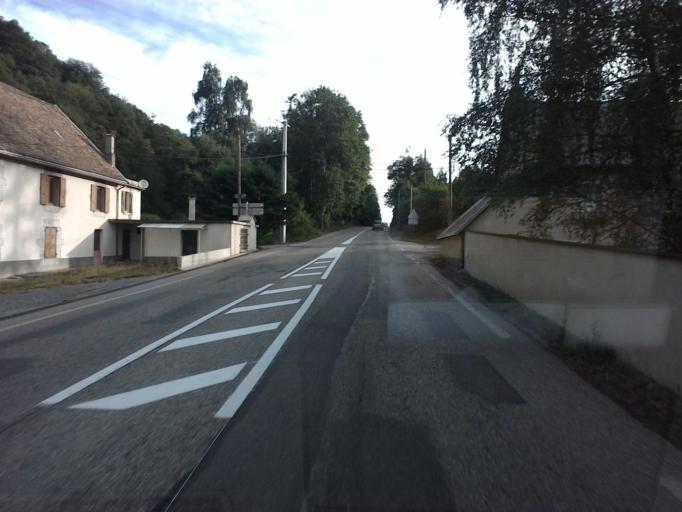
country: FR
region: Rhone-Alpes
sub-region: Departement de l'Isere
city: Pierre-Chatel
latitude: 44.9829
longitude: 5.7719
